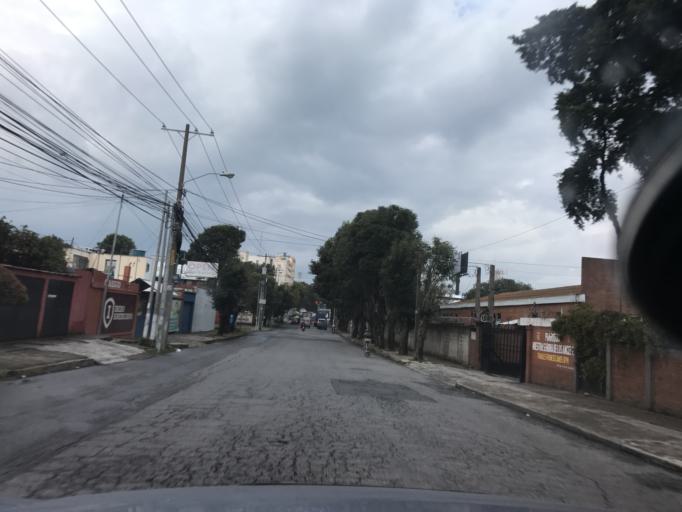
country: GT
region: Guatemala
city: Santa Catarina Pinula
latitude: 14.5841
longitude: -90.5448
